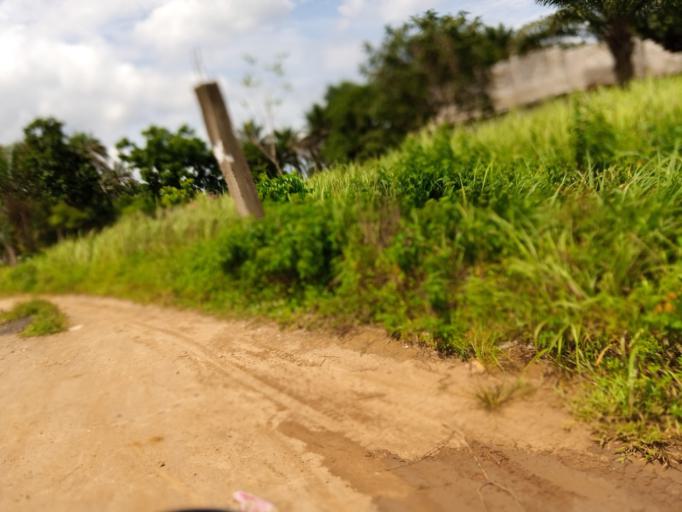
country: SL
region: Northern Province
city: Masoyila
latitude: 8.5445
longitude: -13.1546
